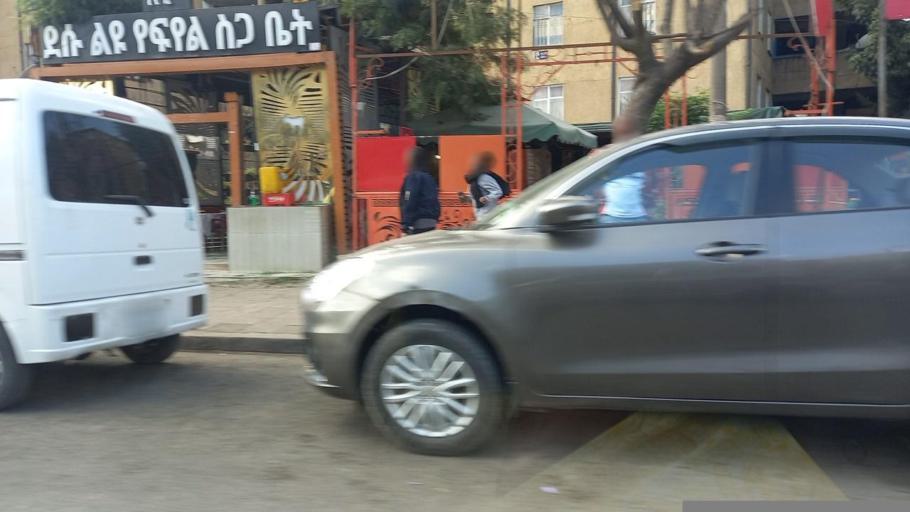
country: ET
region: Adis Abeba
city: Addis Ababa
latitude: 8.9555
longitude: 38.7135
